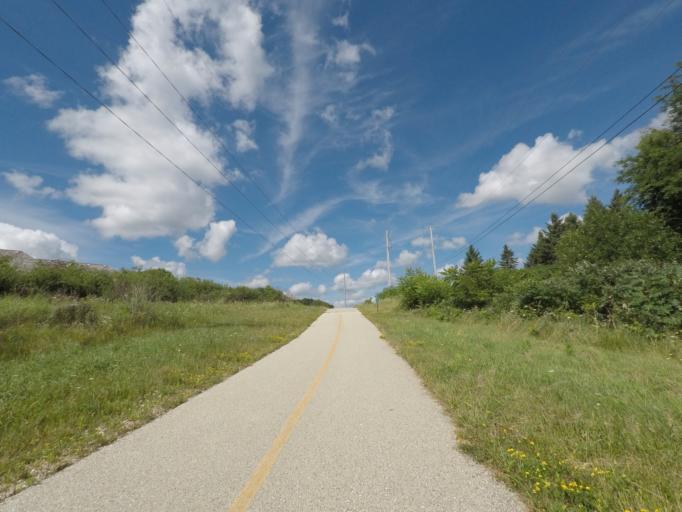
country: US
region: Wisconsin
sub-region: Waukesha County
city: Delafield
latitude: 43.0562
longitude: -88.3598
